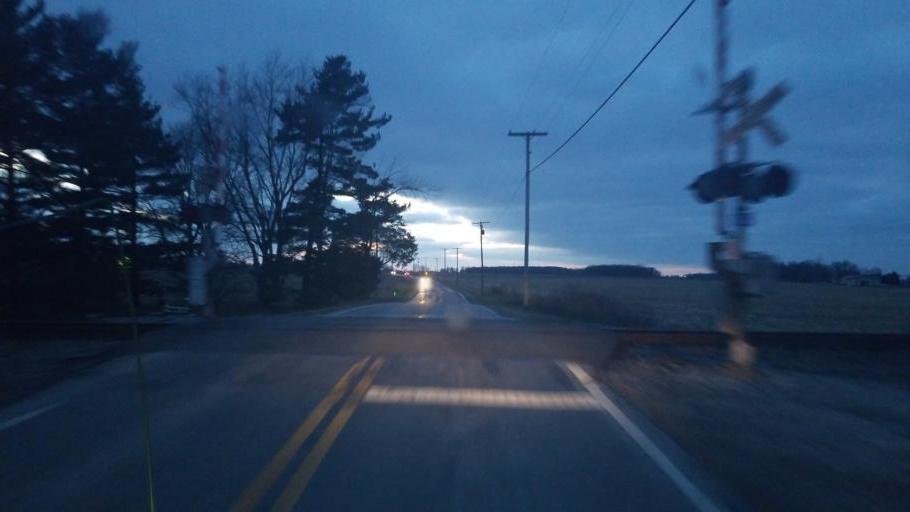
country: US
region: Ohio
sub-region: Marion County
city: Prospect
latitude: 40.4348
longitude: -83.0868
